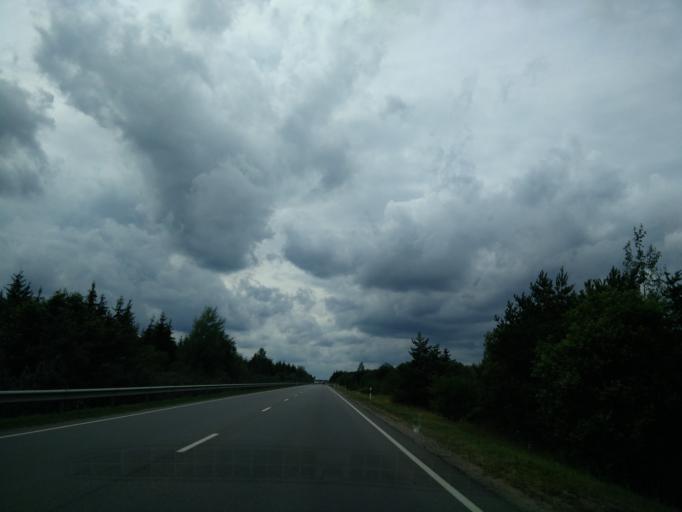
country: LT
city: Trakai
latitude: 54.6253
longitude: 24.9915
